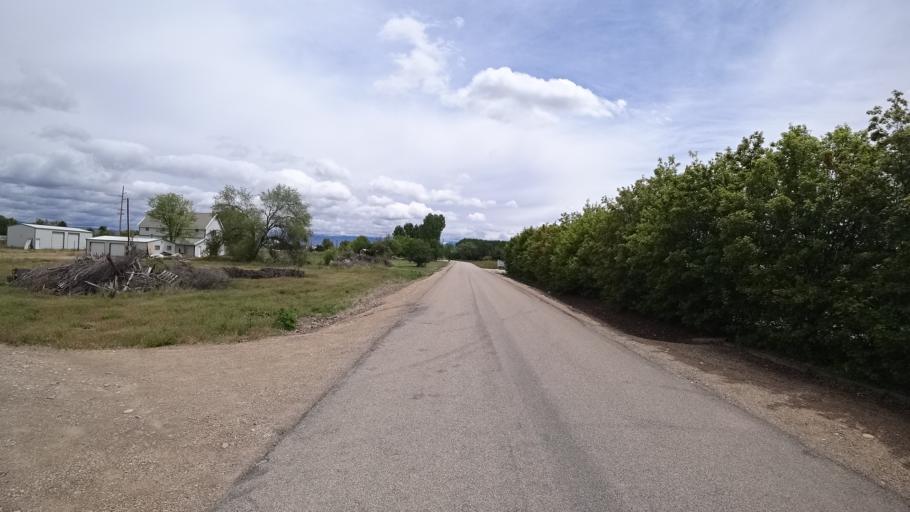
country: US
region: Idaho
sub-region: Ada County
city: Eagle
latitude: 43.6934
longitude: -116.4108
